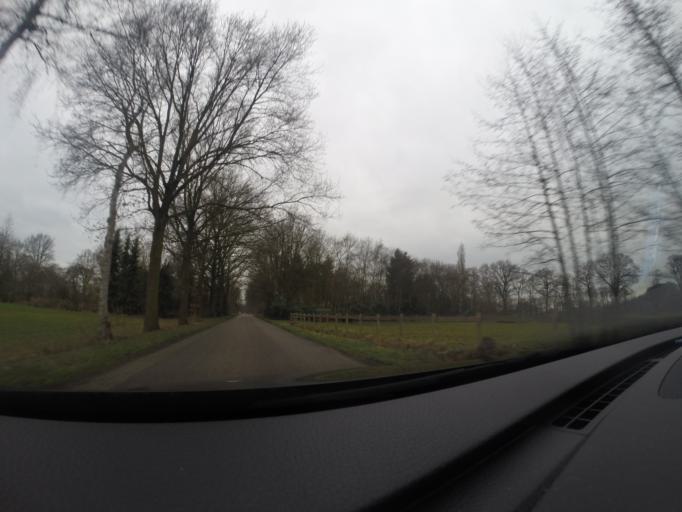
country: NL
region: Overijssel
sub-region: Gemeente Haaksbergen
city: Haaksbergen
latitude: 52.1604
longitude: 6.7636
